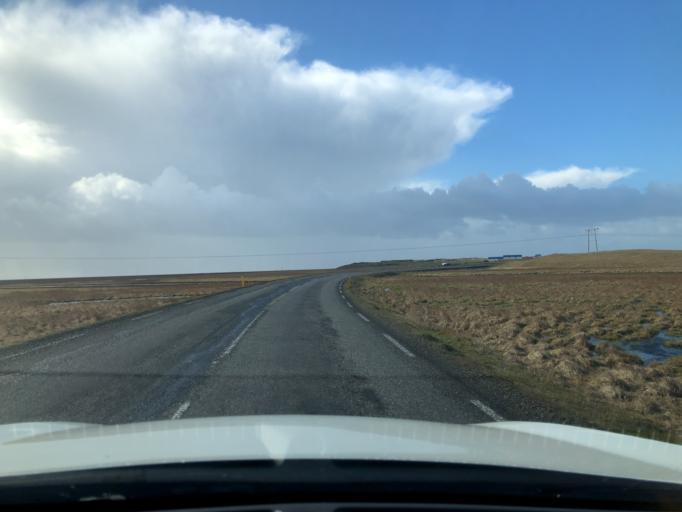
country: IS
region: East
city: Hoefn
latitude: 64.3108
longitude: -15.4061
